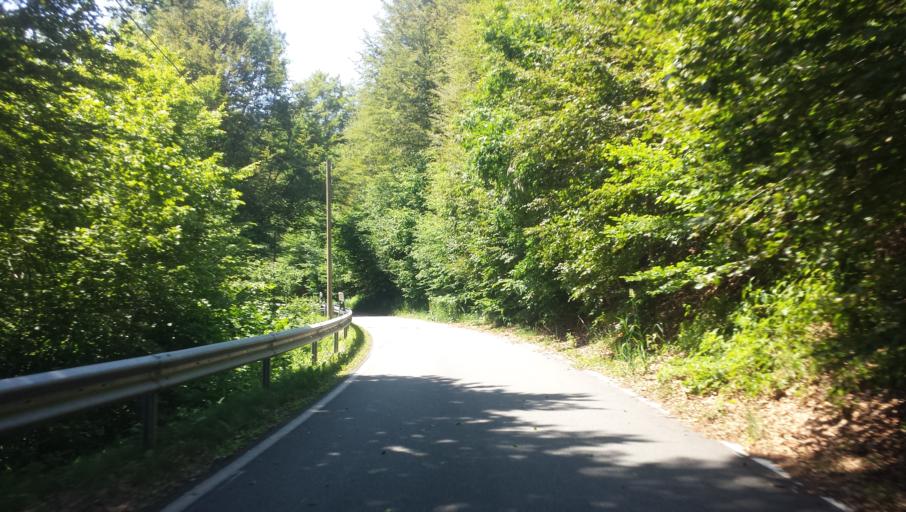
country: DE
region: Rheinland-Pfalz
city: Waldleiningen
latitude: 49.3424
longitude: 7.8610
